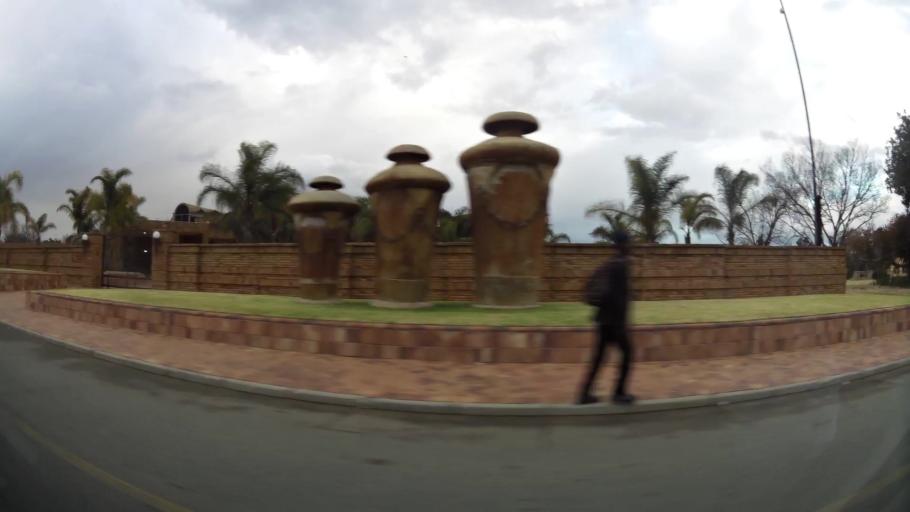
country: ZA
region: Orange Free State
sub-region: Lejweleputswa District Municipality
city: Welkom
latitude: -27.9577
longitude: 26.7365
